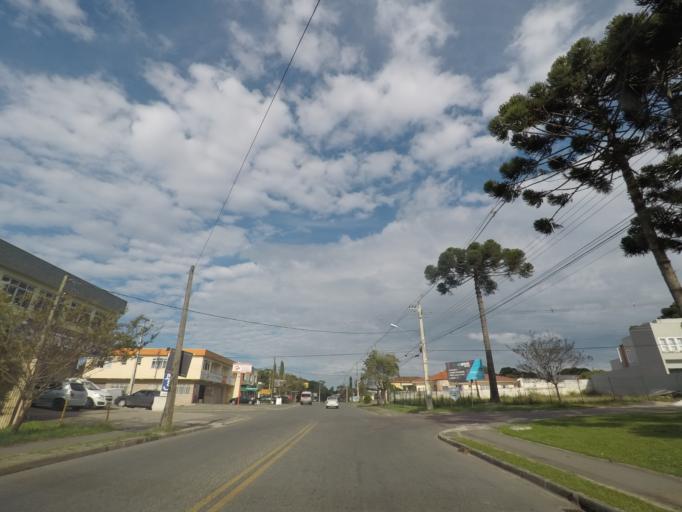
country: BR
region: Parana
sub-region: Sao Jose Dos Pinhais
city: Sao Jose dos Pinhais
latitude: -25.5652
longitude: -49.2890
